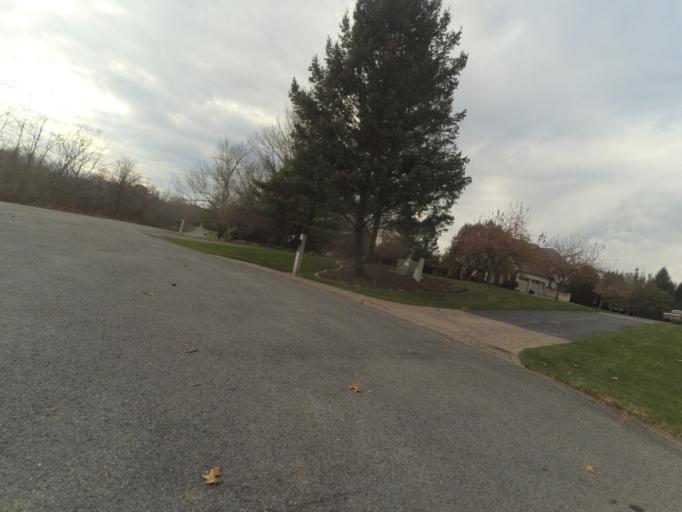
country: US
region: Pennsylvania
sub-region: Centre County
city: Boalsburg
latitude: 40.7798
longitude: -77.8094
